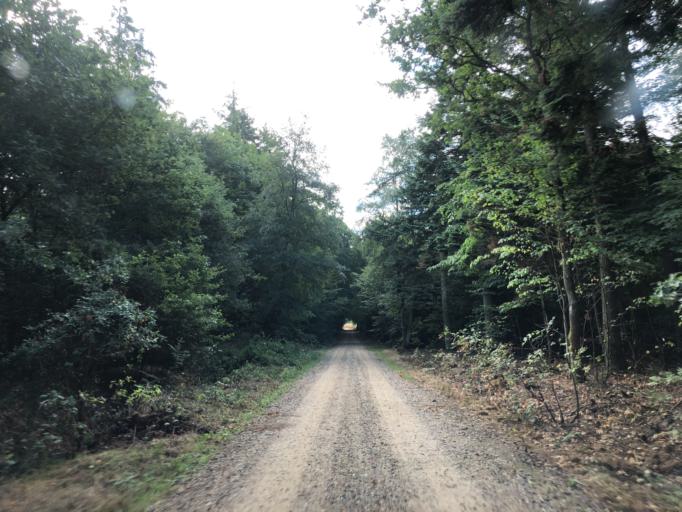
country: DK
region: Central Jutland
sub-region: Holstebro Kommune
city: Ulfborg
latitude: 56.1649
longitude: 8.4007
